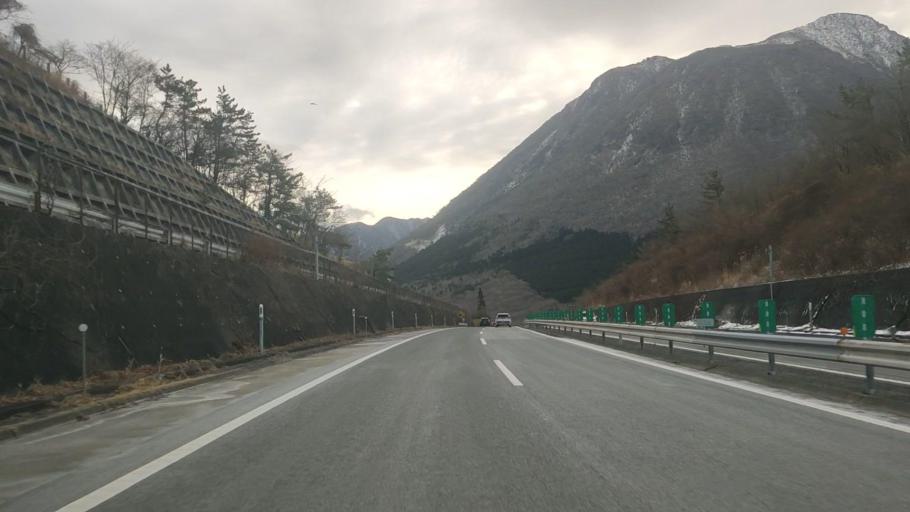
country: JP
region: Oita
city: Beppu
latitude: 33.2960
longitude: 131.3657
